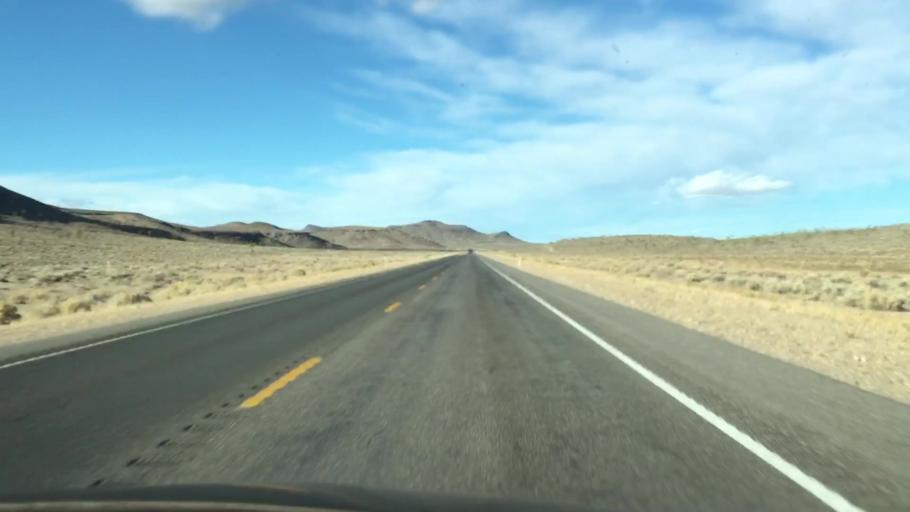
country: US
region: Nevada
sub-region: Esmeralda County
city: Goldfield
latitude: 37.6294
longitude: -117.2184
